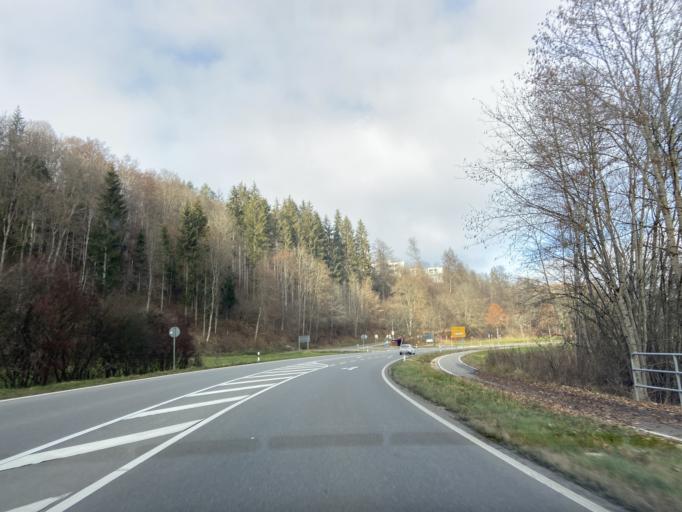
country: DE
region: Baden-Wuerttemberg
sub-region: Tuebingen Region
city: Gammertingen
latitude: 48.2719
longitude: 9.2135
